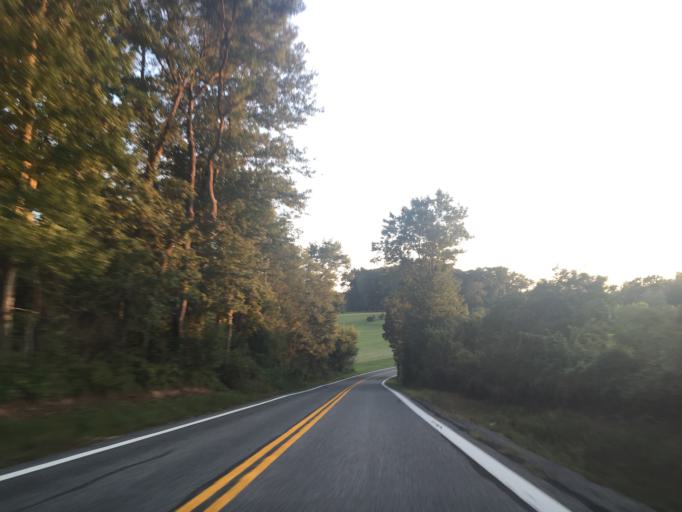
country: US
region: Pennsylvania
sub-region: York County
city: Susquehanna Trails
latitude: 39.6805
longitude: -76.3083
